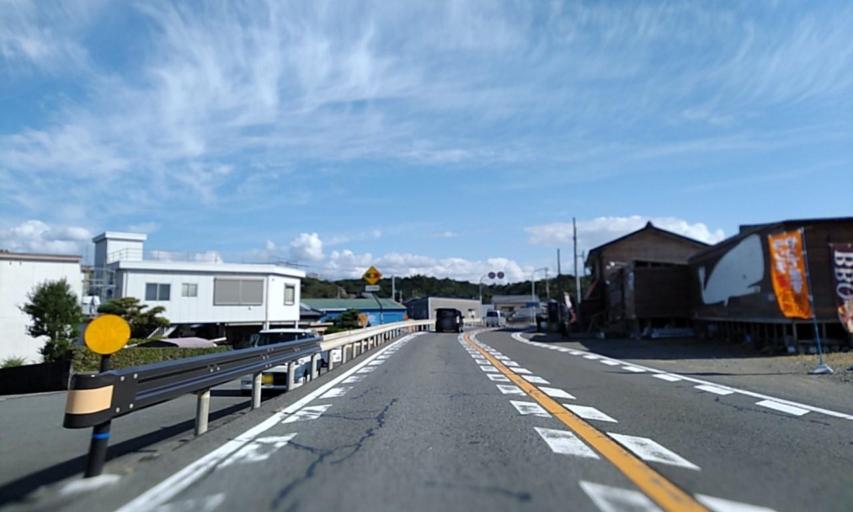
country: JP
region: Wakayama
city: Gobo
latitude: 33.8087
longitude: 135.2202
